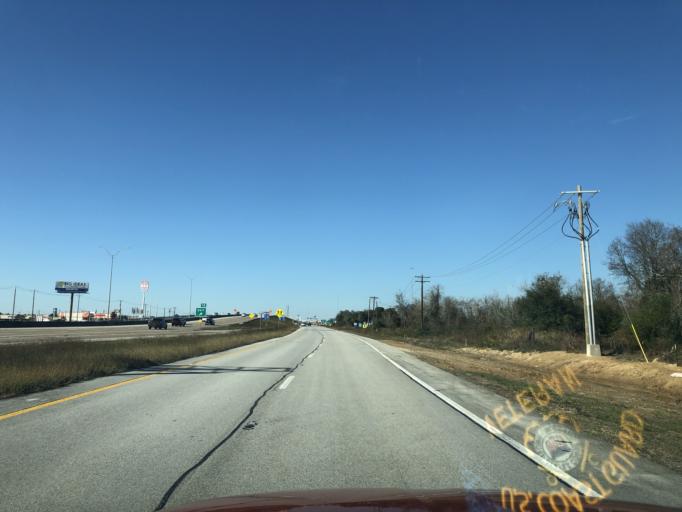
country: US
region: Texas
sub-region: Galveston County
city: Hitchcock
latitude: 29.3995
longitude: -95.0294
